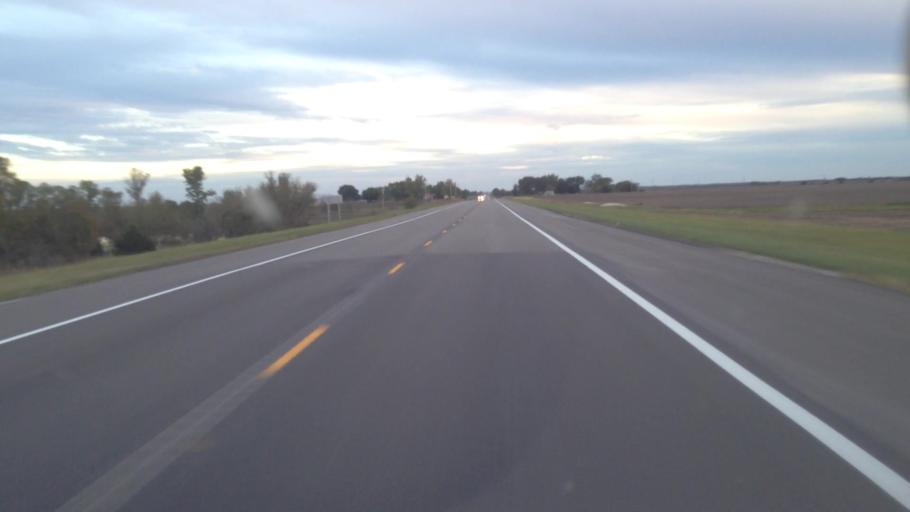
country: US
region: Kansas
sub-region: Anderson County
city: Garnett
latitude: 38.3900
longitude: -95.2488
